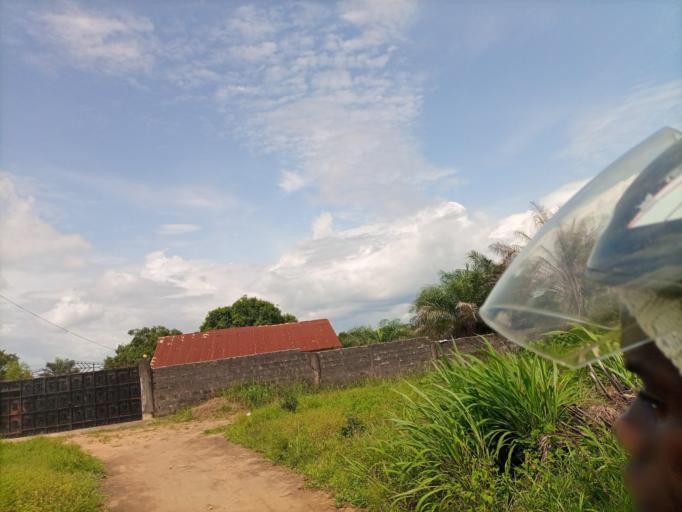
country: SL
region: Northern Province
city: Masoyila
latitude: 8.5414
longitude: -13.1477
